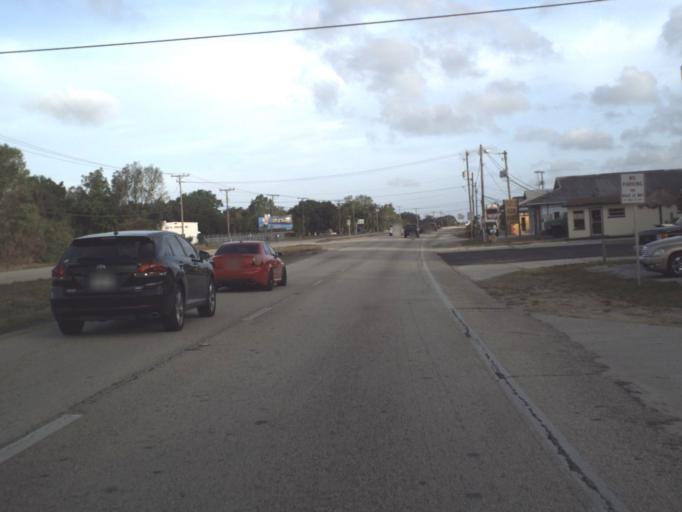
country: US
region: Florida
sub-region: Brevard County
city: Rockledge
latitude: 28.3200
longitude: -80.7137
